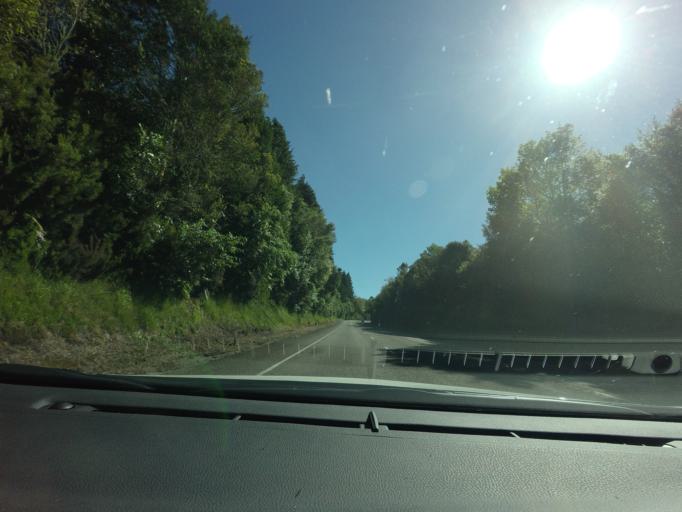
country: NZ
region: Bay of Plenty
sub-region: Rotorua District
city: Rotorua
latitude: -38.0747
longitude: 176.1651
